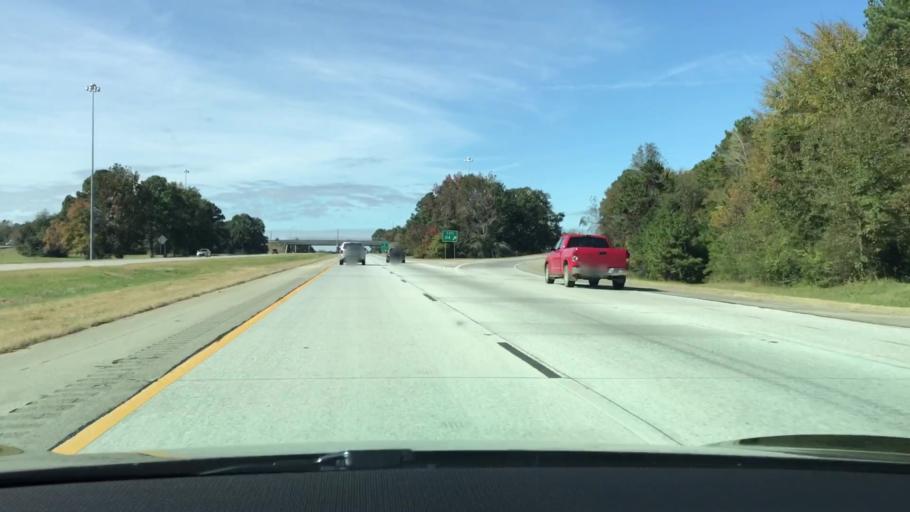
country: US
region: Georgia
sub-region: Morgan County
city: Madison
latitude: 33.5551
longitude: -83.4681
